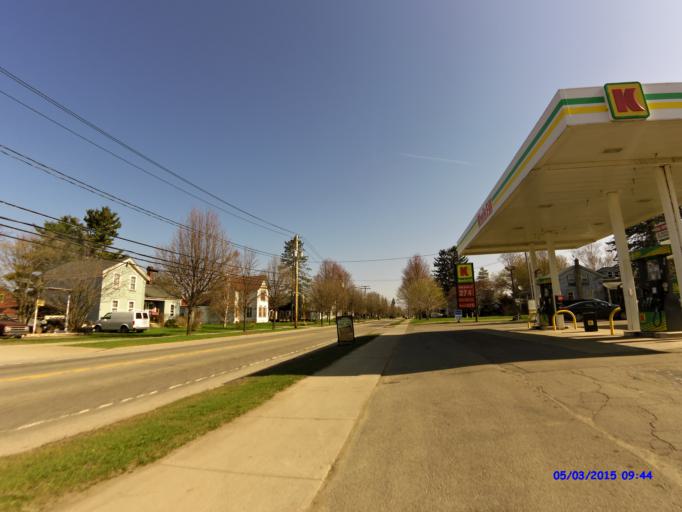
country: US
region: New York
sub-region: Cattaraugus County
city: Franklinville
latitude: 42.3307
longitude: -78.4600
